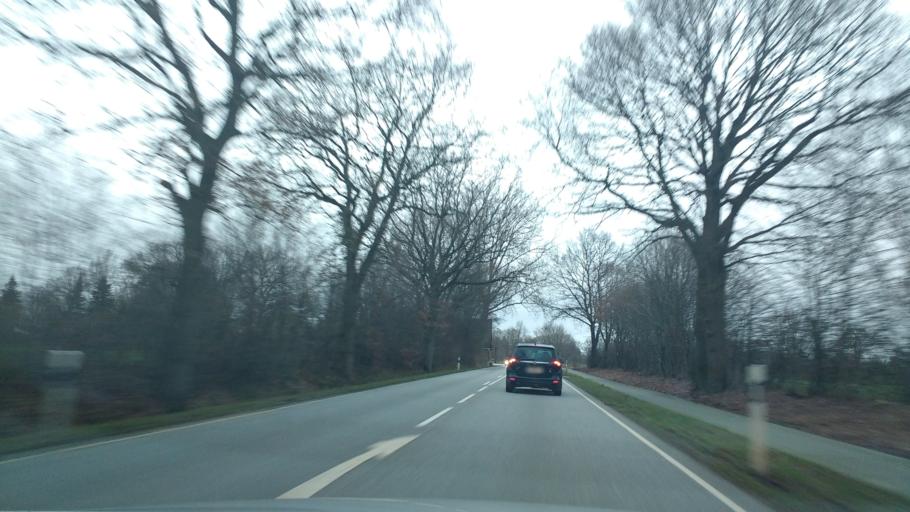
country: DE
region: Schleswig-Holstein
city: Oelixdorf
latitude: 53.9551
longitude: 9.5574
